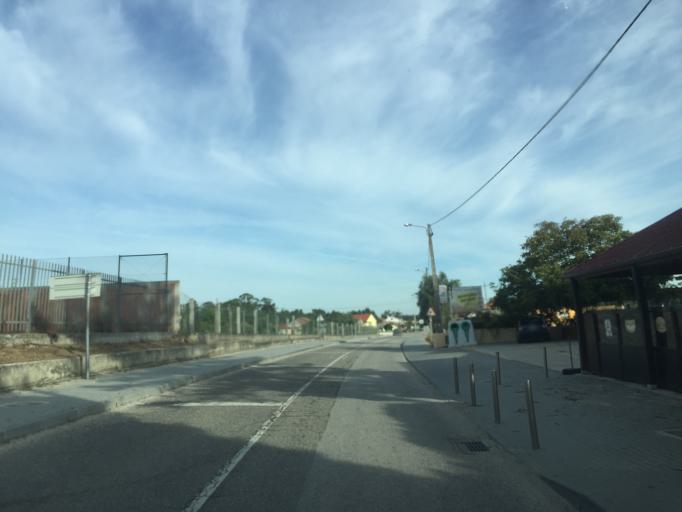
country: PT
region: Leiria
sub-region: Leiria
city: Monte Redondo
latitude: 39.9529
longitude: -8.7860
